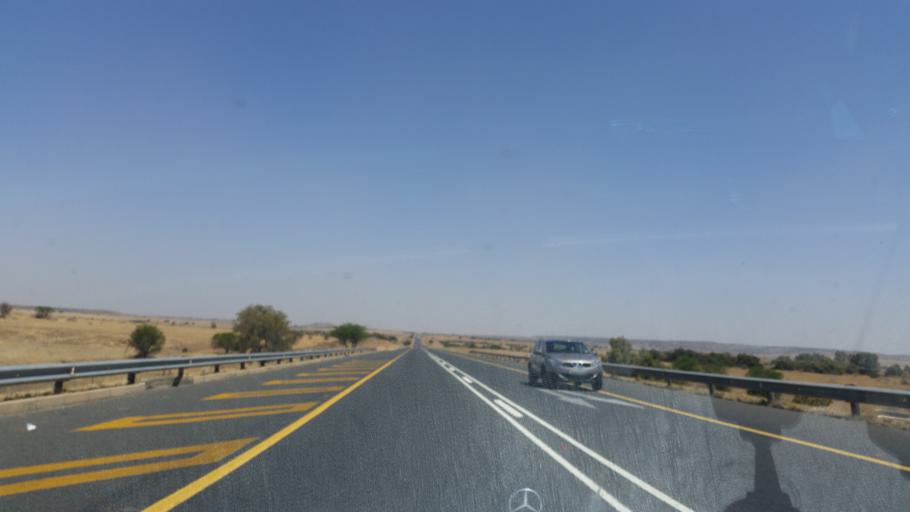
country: ZA
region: Orange Free State
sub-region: Lejweleputswa District Municipality
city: Winburg
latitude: -28.6693
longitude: 26.8473
